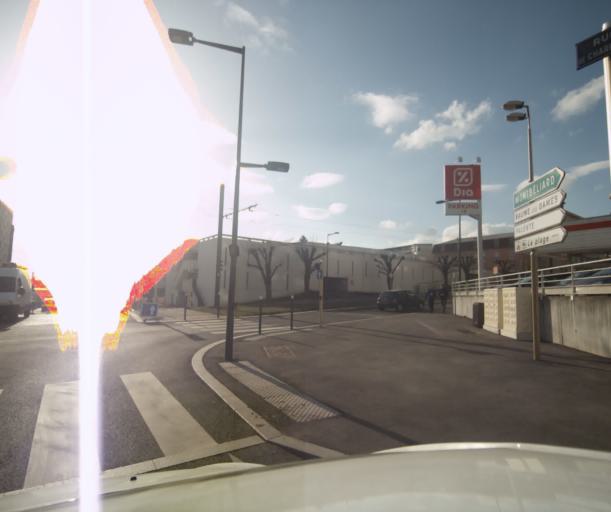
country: FR
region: Franche-Comte
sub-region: Departement du Doubs
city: Besancon
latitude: 47.2563
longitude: 6.0448
